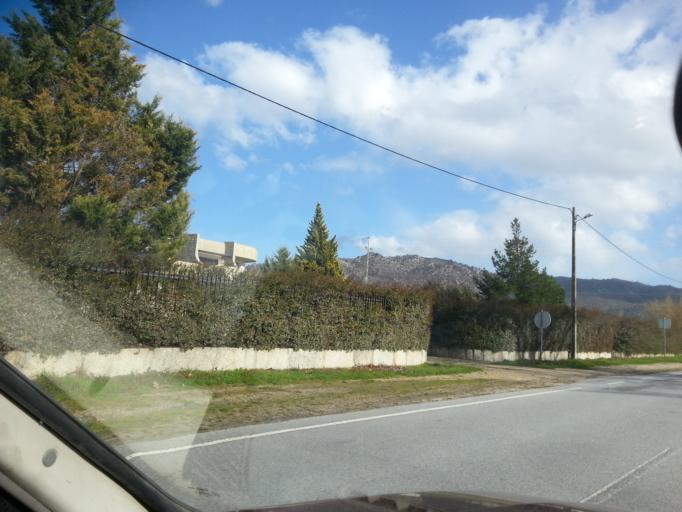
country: PT
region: Guarda
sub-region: Guarda
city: Guarda
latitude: 40.6141
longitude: -7.3059
